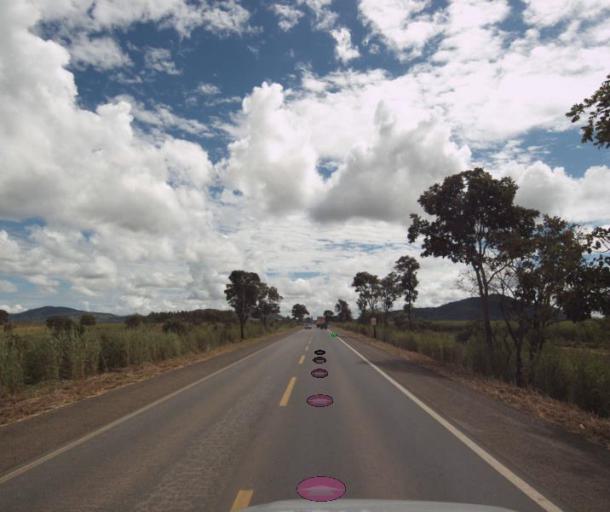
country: BR
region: Goias
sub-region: Uruacu
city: Uruacu
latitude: -14.4362
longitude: -49.1568
